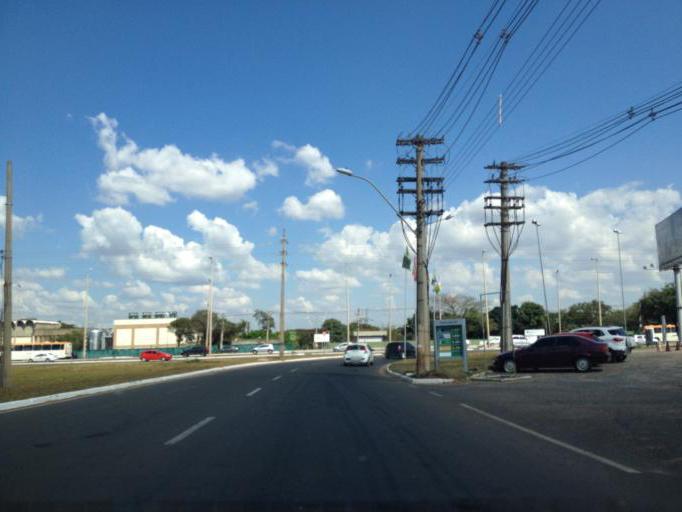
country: BR
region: Federal District
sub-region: Brasilia
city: Brasilia
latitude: -15.8087
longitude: -47.9516
